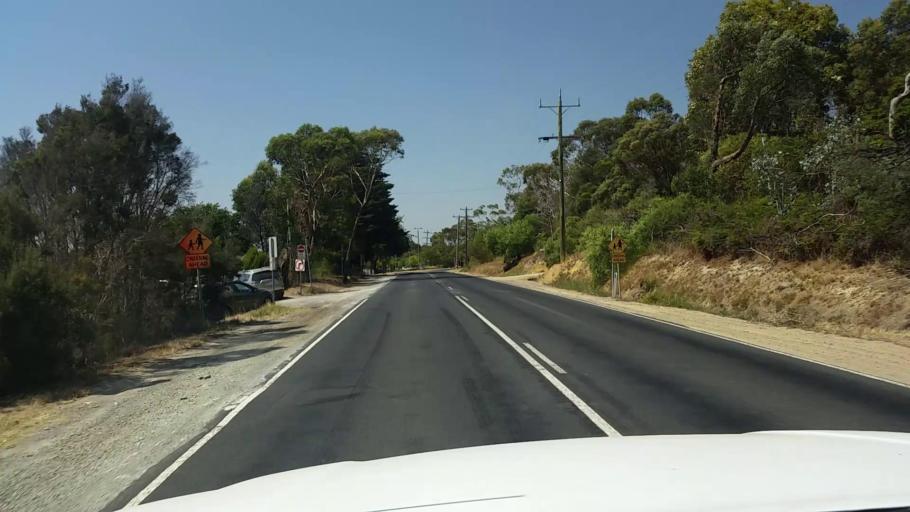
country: AU
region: Victoria
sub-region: Mornington Peninsula
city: Tyabb
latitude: -38.2610
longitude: 145.1646
